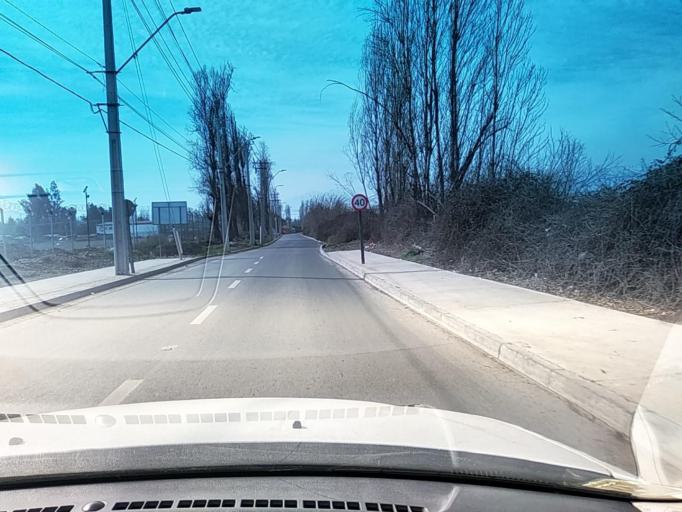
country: CL
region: Santiago Metropolitan
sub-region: Provincia de Chacabuco
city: Chicureo Abajo
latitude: -33.2859
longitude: -70.7318
